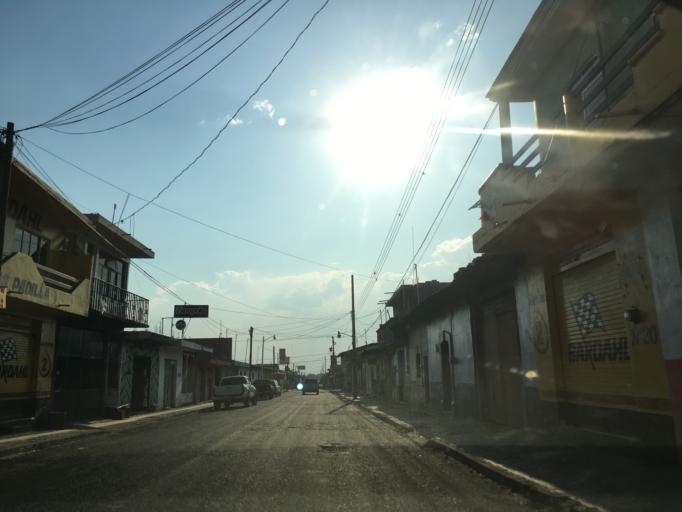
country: MX
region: Michoacan
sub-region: Indaparapeo
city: Colonia de Guadalupe
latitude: 19.8090
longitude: -100.8876
